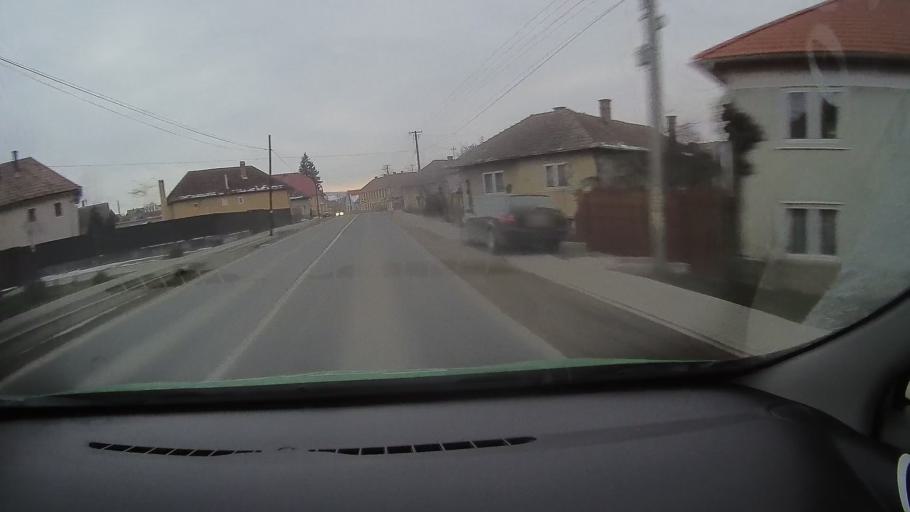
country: RO
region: Harghita
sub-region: Comuna Feliceni
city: Feliceni
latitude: 46.2751
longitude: 25.2836
